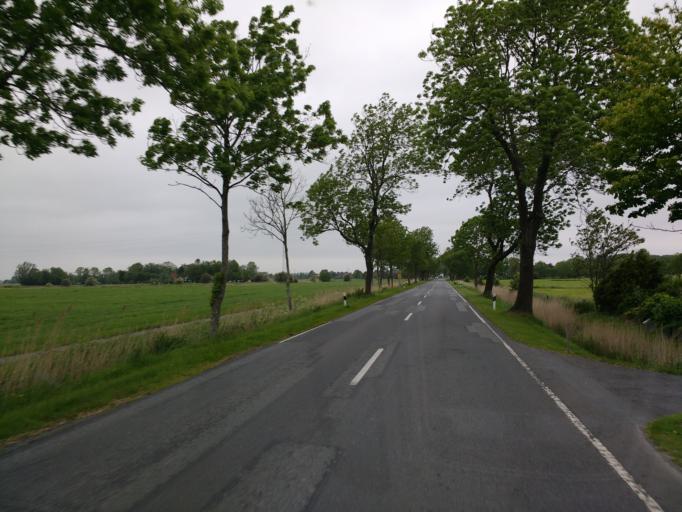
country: DE
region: Lower Saxony
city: Jever
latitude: 53.6536
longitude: 7.9169
